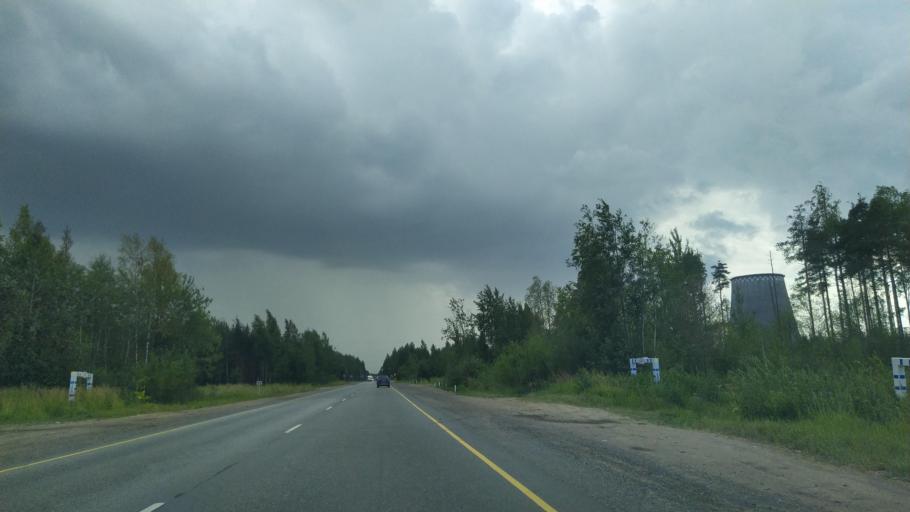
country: RU
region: Leningrad
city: Novoye Devyatkino
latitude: 60.0813
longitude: 30.4968
